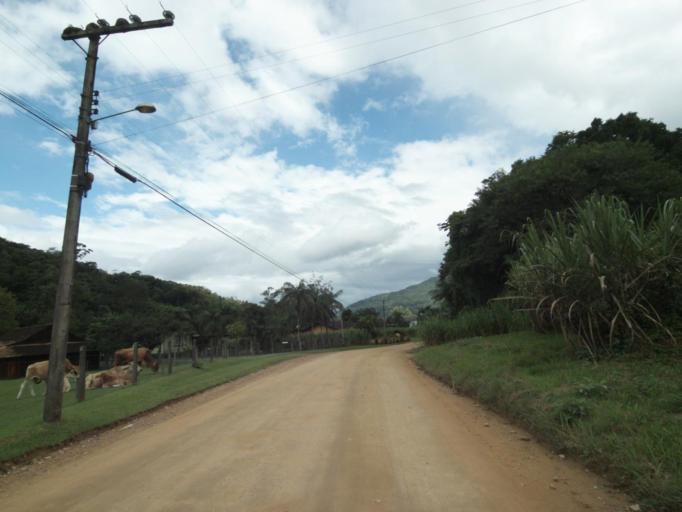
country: BR
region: Santa Catarina
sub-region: Pomerode
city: Pomerode
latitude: -26.7115
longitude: -49.2093
